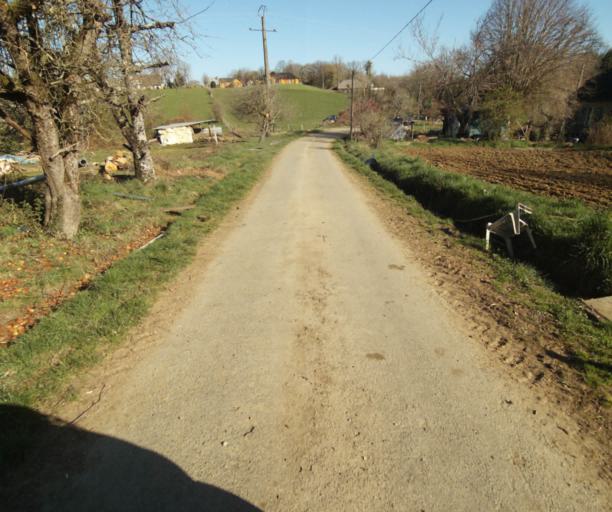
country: FR
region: Limousin
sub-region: Departement de la Correze
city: Seilhac
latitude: 45.3802
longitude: 1.7639
